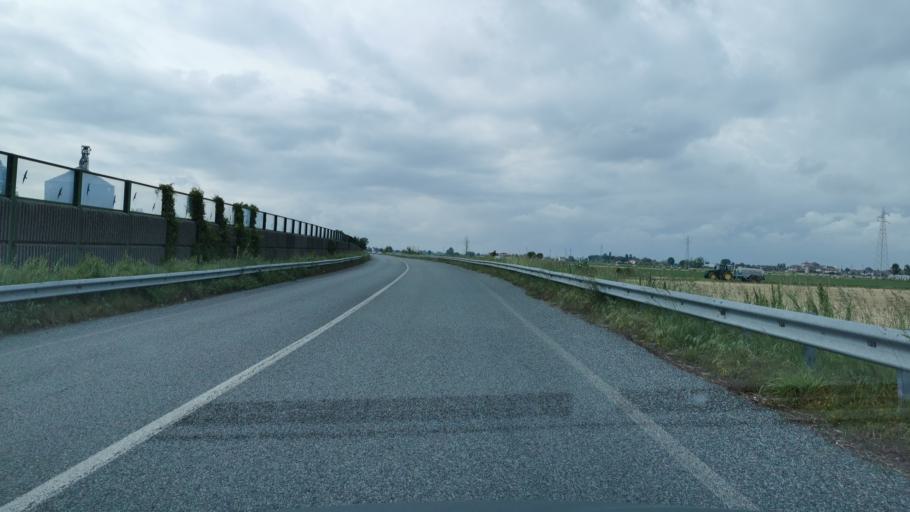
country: IT
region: Piedmont
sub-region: Provincia di Cuneo
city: Racconigi
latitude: 44.7855
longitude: 7.6992
